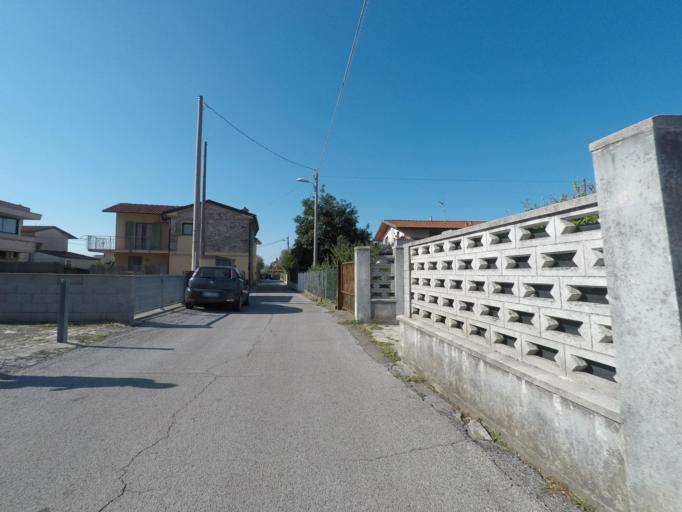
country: IT
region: Tuscany
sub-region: Provincia di Massa-Carrara
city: Massa
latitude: 44.0351
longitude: 10.1325
